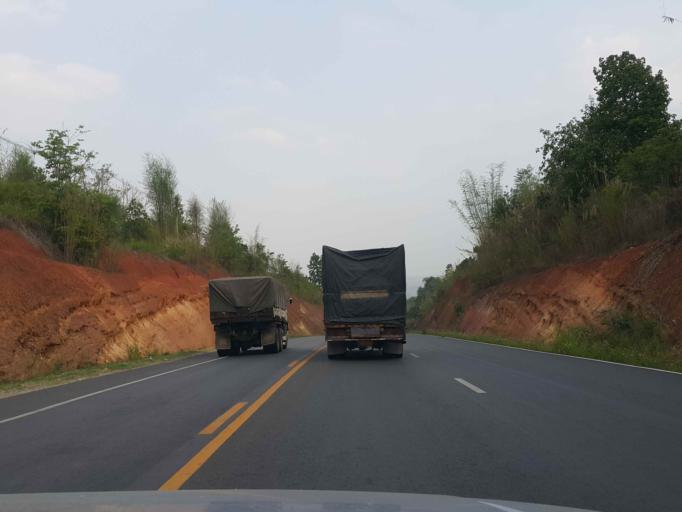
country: TH
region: Chiang Mai
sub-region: Amphoe Chiang Dao
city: Chiang Dao
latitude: 19.3637
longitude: 98.9517
